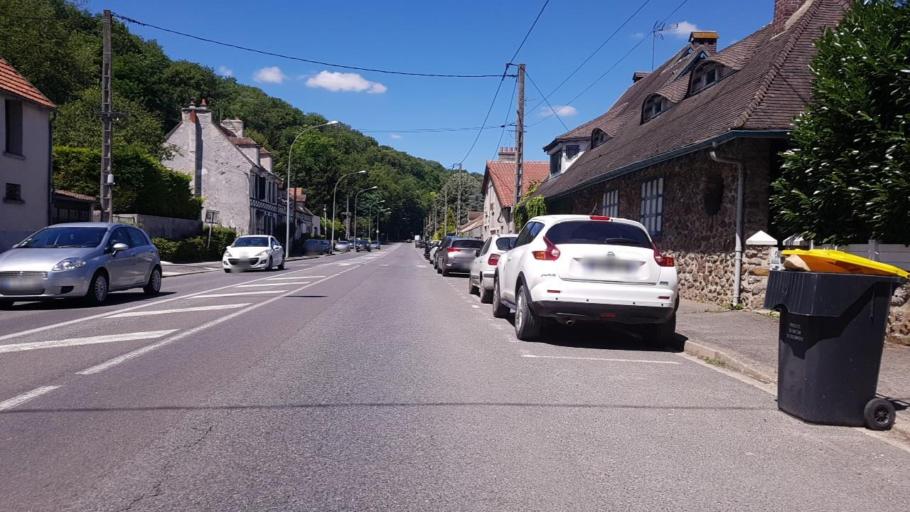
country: FR
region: Ile-de-France
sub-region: Departement de Seine-et-Marne
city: Saint-Jean-les-Deux-Jumeaux
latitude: 48.9529
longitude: 3.0107
